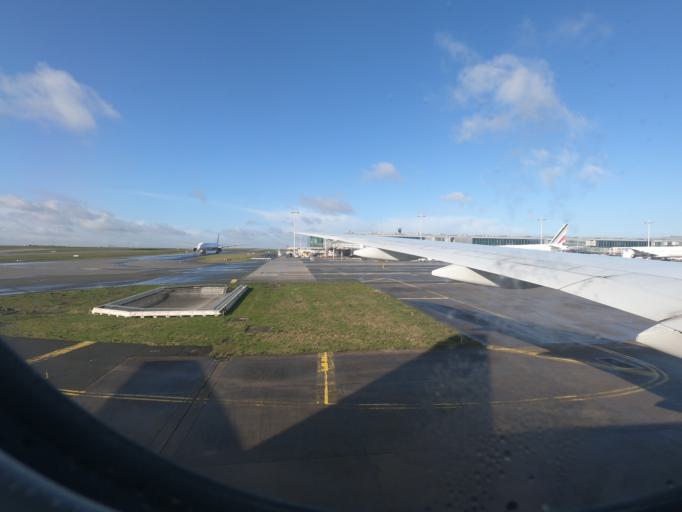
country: FR
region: Ile-de-France
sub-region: Departement de Seine-et-Marne
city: Mitry-Mory
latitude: 49.0011
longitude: 2.5889
